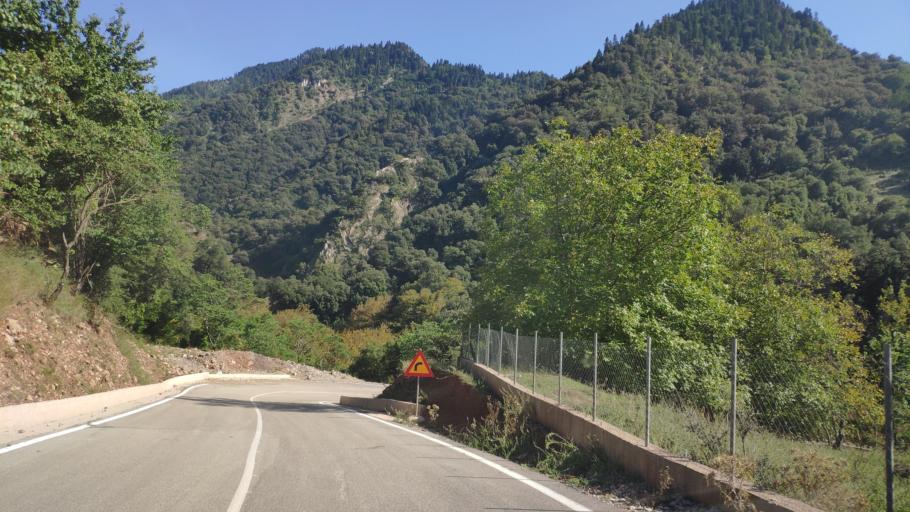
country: GR
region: Central Greece
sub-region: Nomos Evrytanias
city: Kerasochori
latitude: 39.0903
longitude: 21.6046
